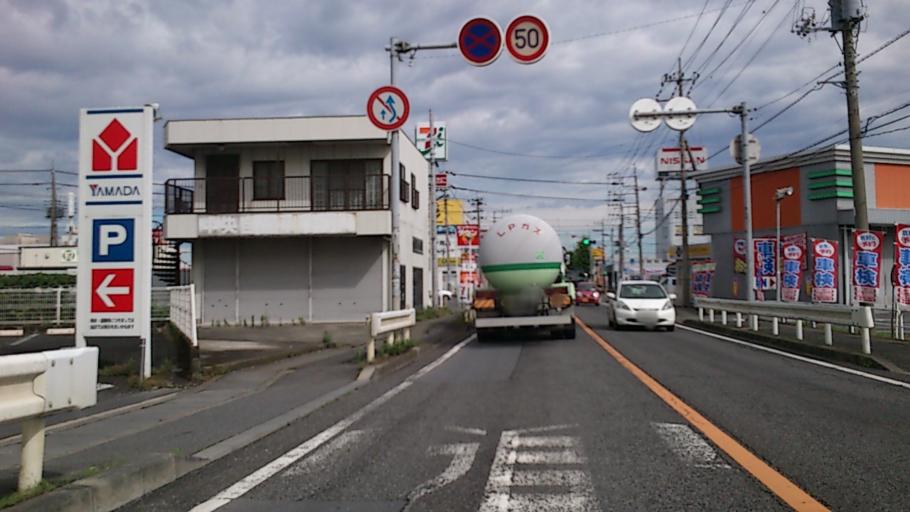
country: JP
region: Saitama
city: Honjo
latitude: 36.2417
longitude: 139.2013
